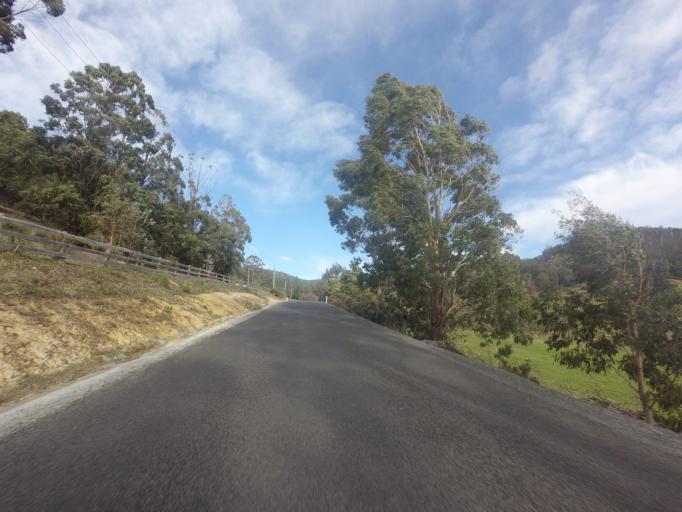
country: AU
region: Tasmania
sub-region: Kingborough
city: Margate
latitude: -42.9920
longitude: 147.1861
